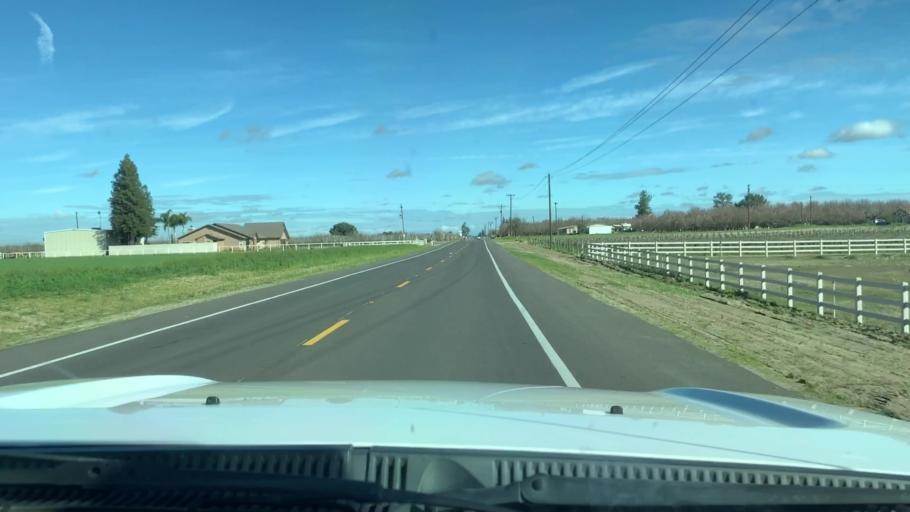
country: US
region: California
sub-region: Fresno County
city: Laton
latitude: 36.4967
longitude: -119.6830
